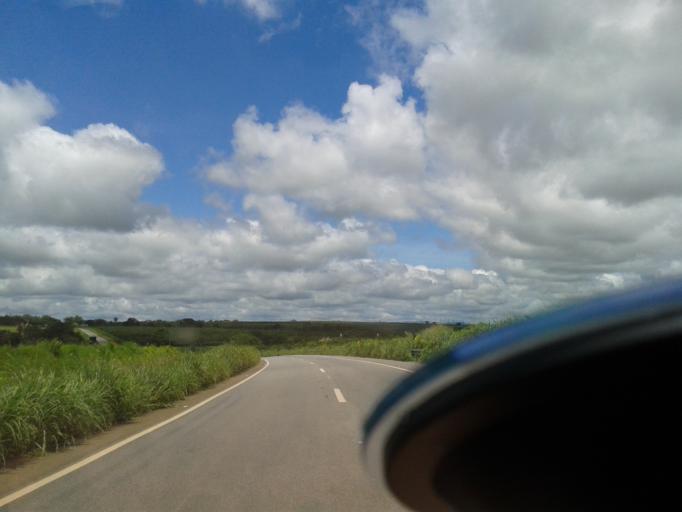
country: BR
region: Goias
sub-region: Itaberai
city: Itaberai
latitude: -16.0712
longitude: -49.7572
